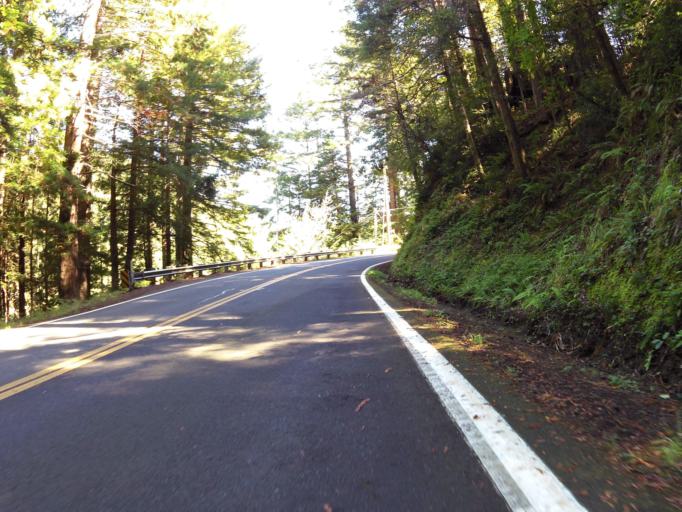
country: US
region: California
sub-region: Mendocino County
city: Fort Bragg
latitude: 39.7333
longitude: -123.8099
